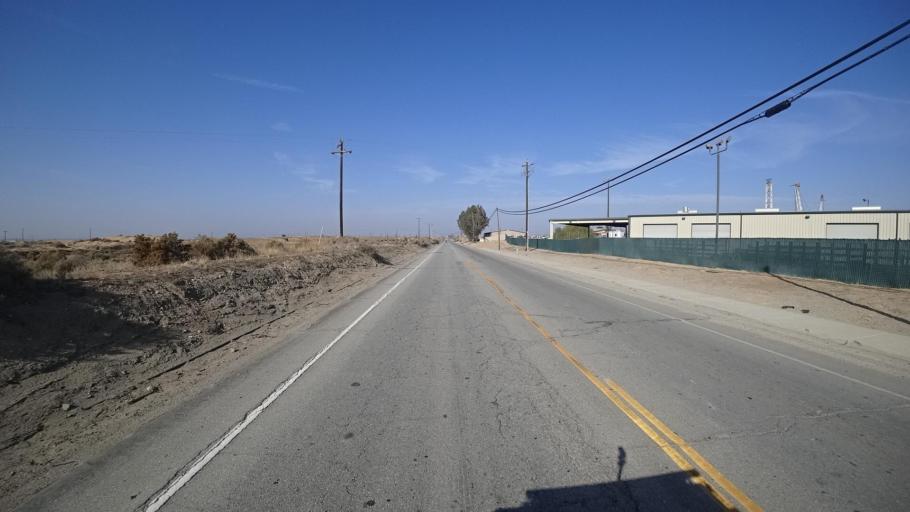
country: US
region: California
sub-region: Kern County
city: Oildale
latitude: 35.4570
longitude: -119.0447
